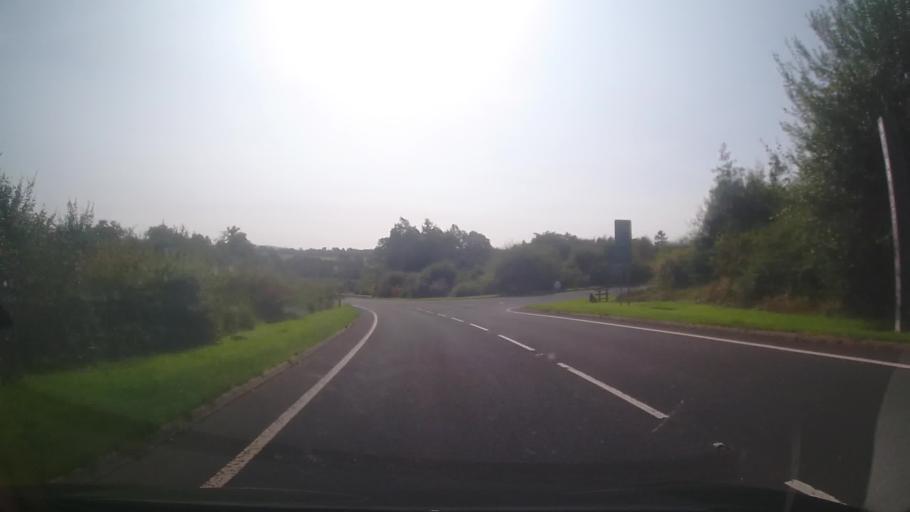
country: GB
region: Wales
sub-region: Sir Powys
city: Llandrindod Wells
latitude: 52.2094
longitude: -3.4401
